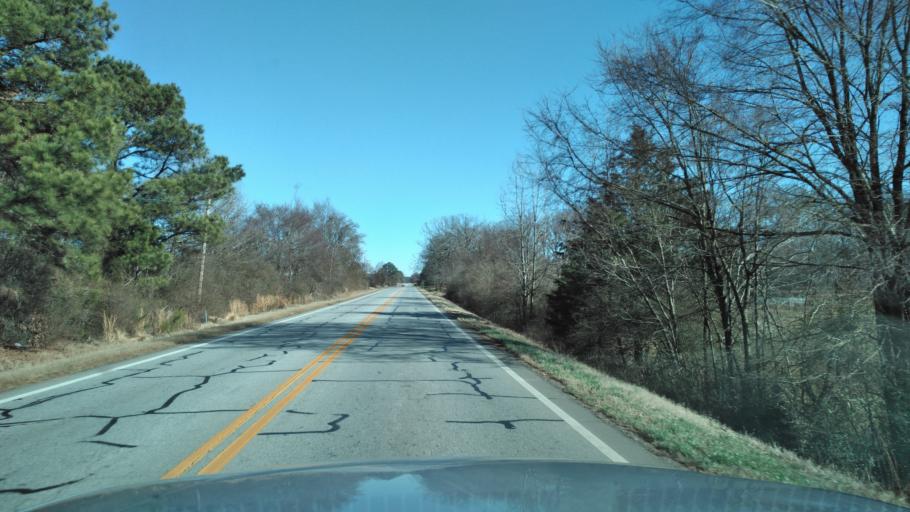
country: US
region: Georgia
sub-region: Banks County
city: Maysville
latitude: 34.2427
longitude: -83.5354
